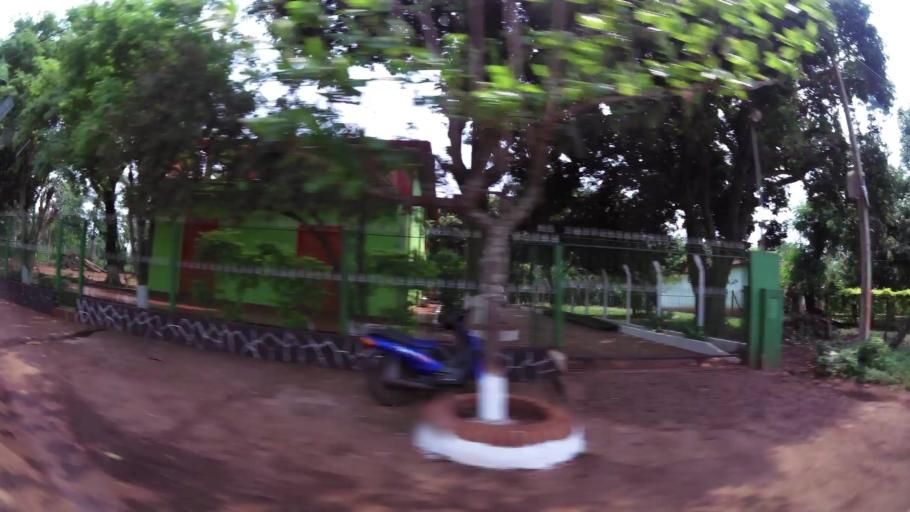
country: AR
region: Misiones
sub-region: Departamento de Iguazu
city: Puerto Iguazu
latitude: -25.5940
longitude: -54.6024
